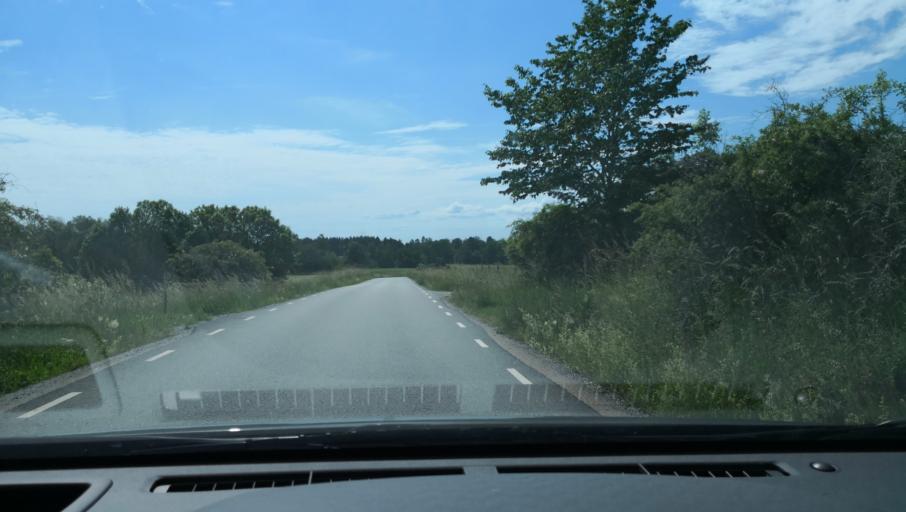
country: SE
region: Uppsala
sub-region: Habo Kommun
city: Balsta
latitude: 59.6876
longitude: 17.4647
